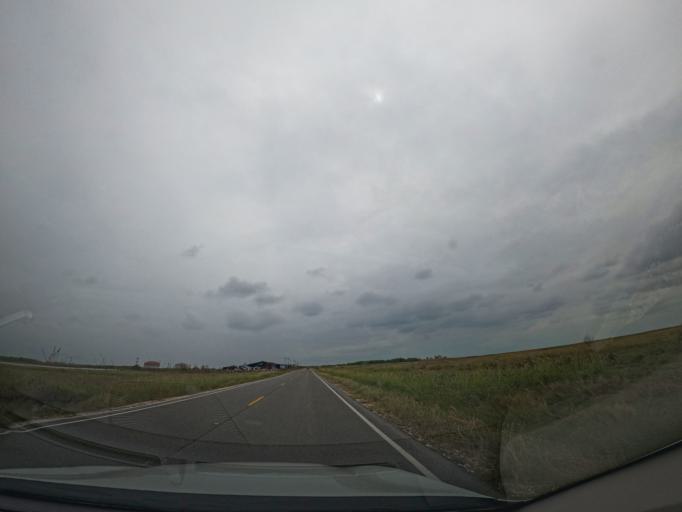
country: US
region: Louisiana
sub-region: Cameron Parish
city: Cameron
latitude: 29.7899
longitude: -93.3493
